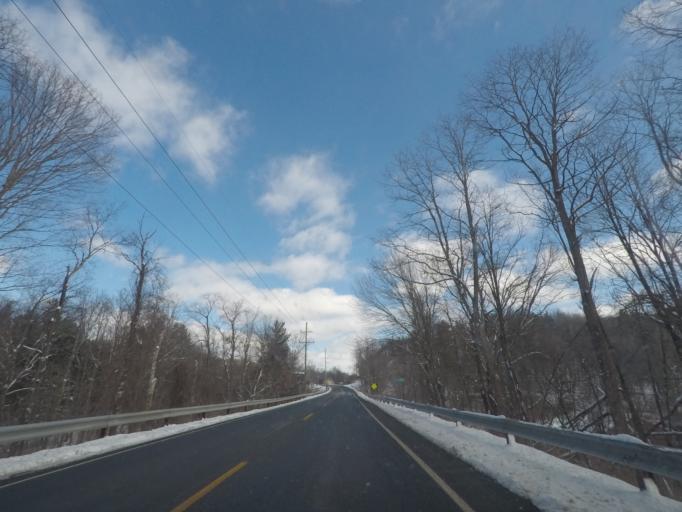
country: US
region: New York
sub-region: Rensselaer County
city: Nassau
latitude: 42.4919
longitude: -73.5159
